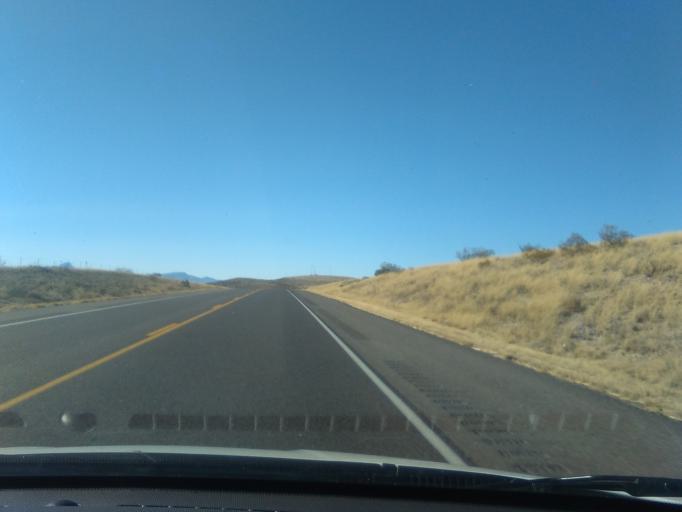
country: US
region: New Mexico
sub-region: Dona Ana County
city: Hatch
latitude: 32.5773
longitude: -107.4377
